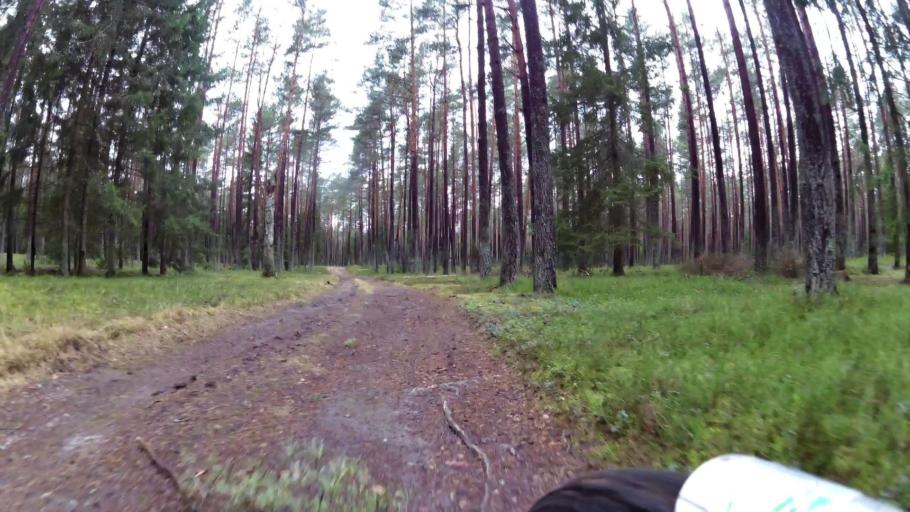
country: PL
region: Pomeranian Voivodeship
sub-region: Powiat bytowski
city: Borzytuchom
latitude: 54.2583
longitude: 17.3722
